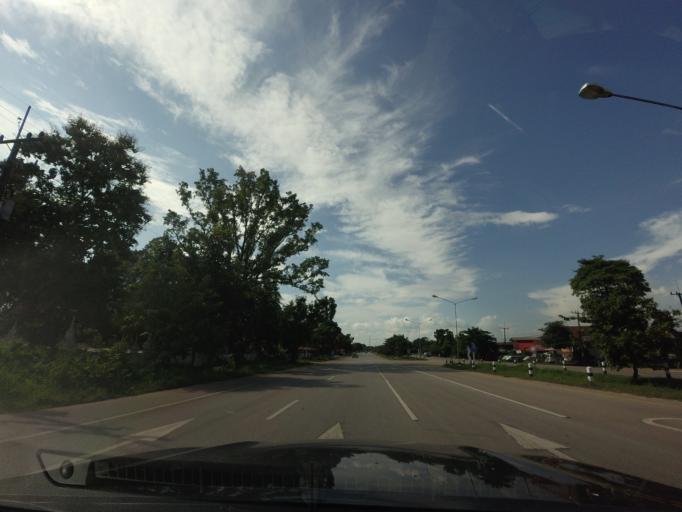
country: TH
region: Nong Khai
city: Sa Khrai
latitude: 17.6776
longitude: 102.7871
